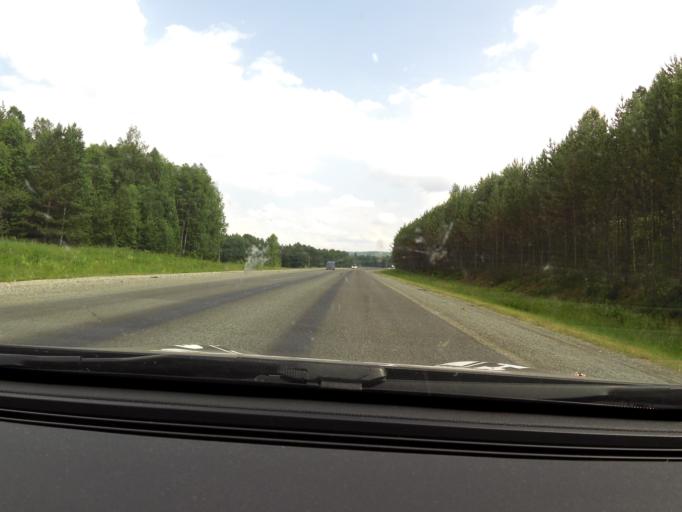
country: RU
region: Sverdlovsk
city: Ufimskiy
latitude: 56.7864
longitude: 58.3867
